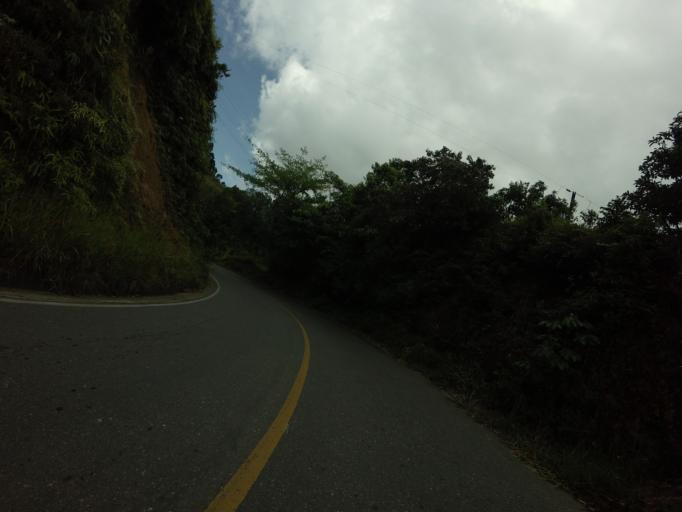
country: CO
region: Caldas
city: Marquetalia
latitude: 5.3035
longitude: -74.9843
